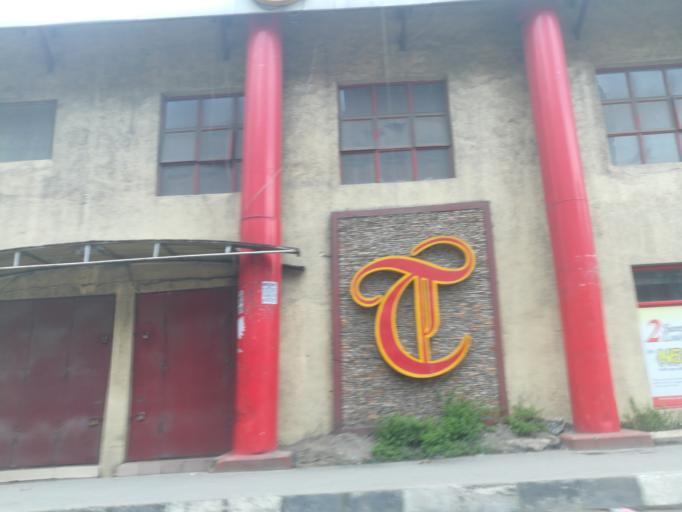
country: NG
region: Lagos
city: Lagos
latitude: 6.4550
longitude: 3.3868
